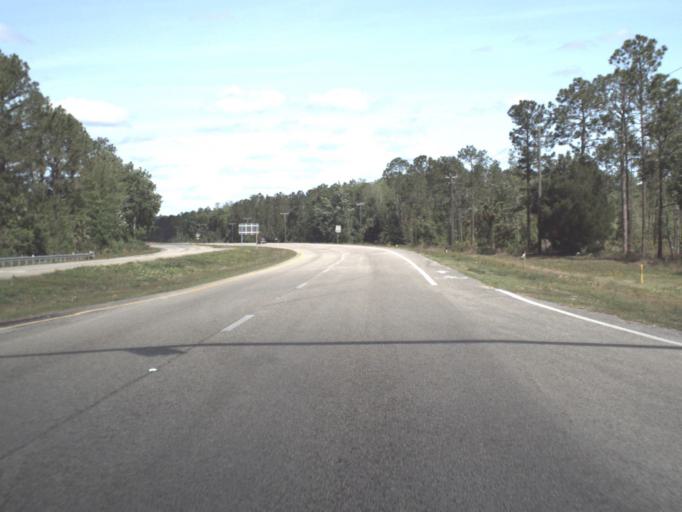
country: US
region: Florida
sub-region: Flagler County
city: Bunnell
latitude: 29.4185
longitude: -81.2097
